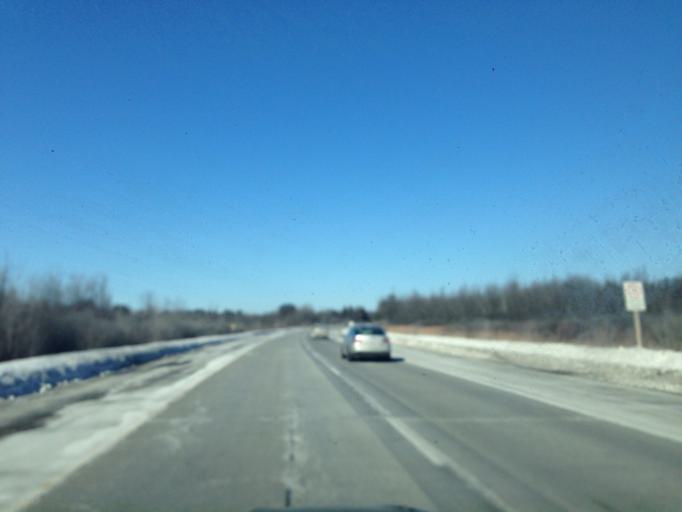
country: CA
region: Ontario
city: Ottawa
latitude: 45.3513
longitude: -75.4567
